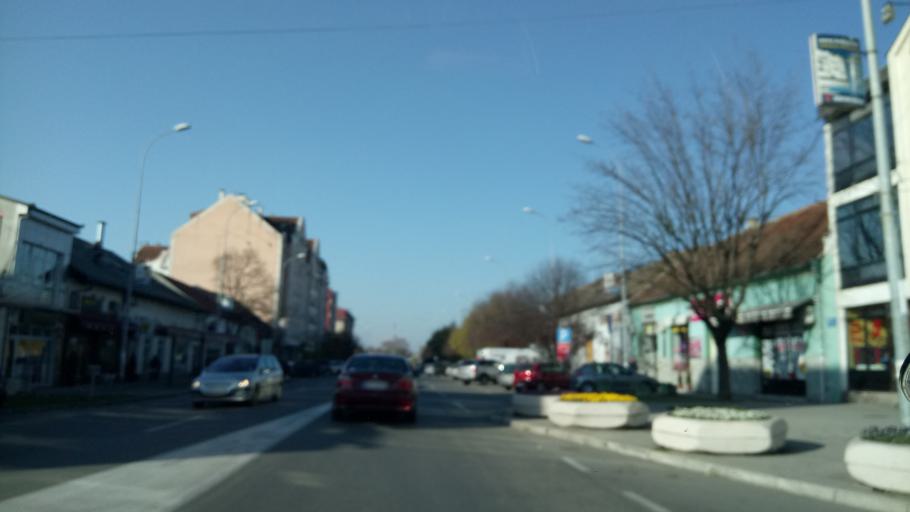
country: RS
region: Autonomna Pokrajina Vojvodina
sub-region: Sremski Okrug
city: Ingija
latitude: 45.0484
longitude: 20.0801
